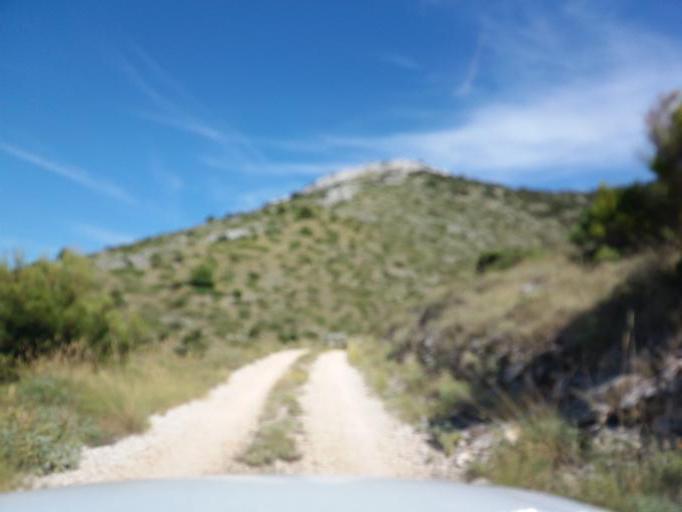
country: HR
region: Zadarska
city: Ugljan
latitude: 44.0164
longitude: 15.0325
